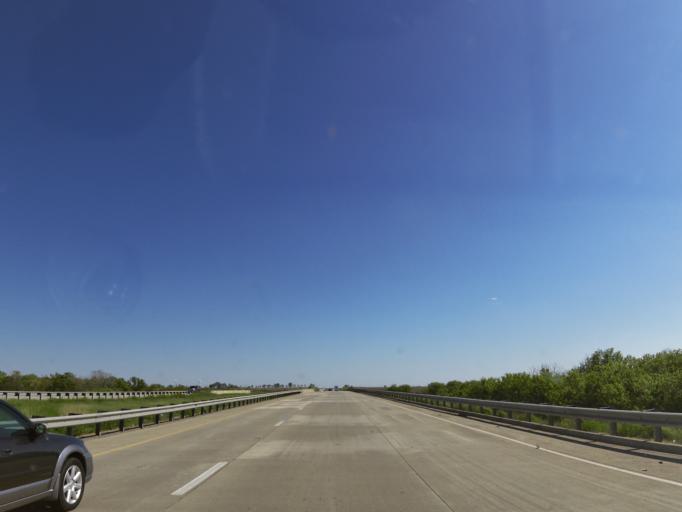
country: US
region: Illinois
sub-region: Ogle County
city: Rochelle
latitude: 41.8475
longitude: -89.0104
